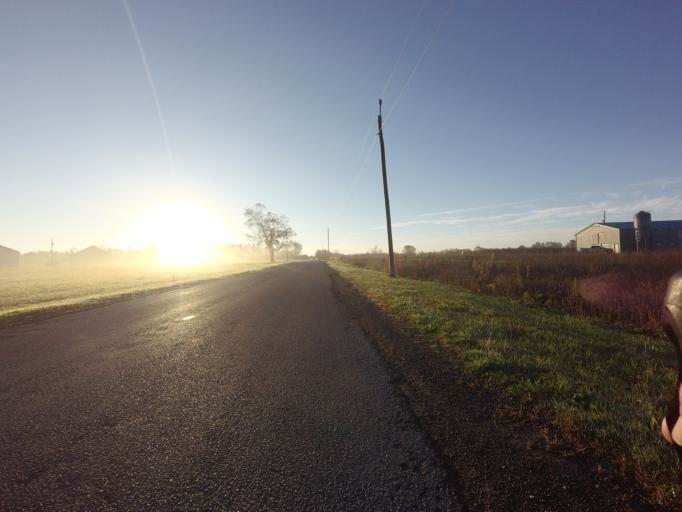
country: CA
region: Ontario
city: Quinte West
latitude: 44.0303
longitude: -77.5663
